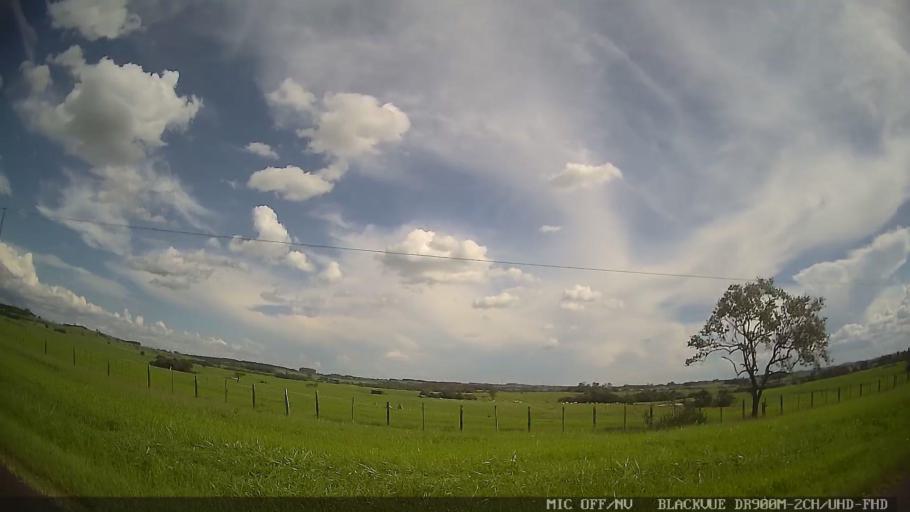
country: BR
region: Sao Paulo
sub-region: Conchas
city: Conchas
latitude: -23.0460
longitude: -47.9510
